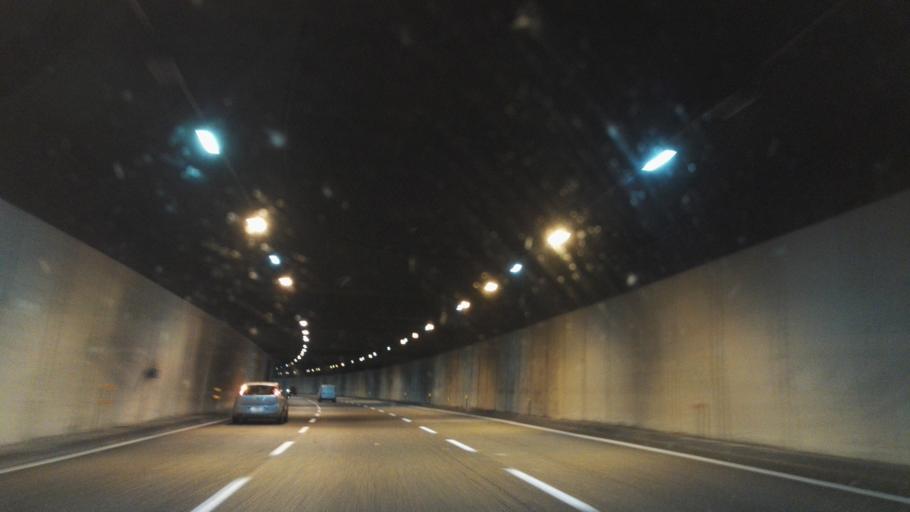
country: IT
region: Lombardy
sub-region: Provincia di Varese
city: Golasecca
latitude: 45.7080
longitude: 8.6509
